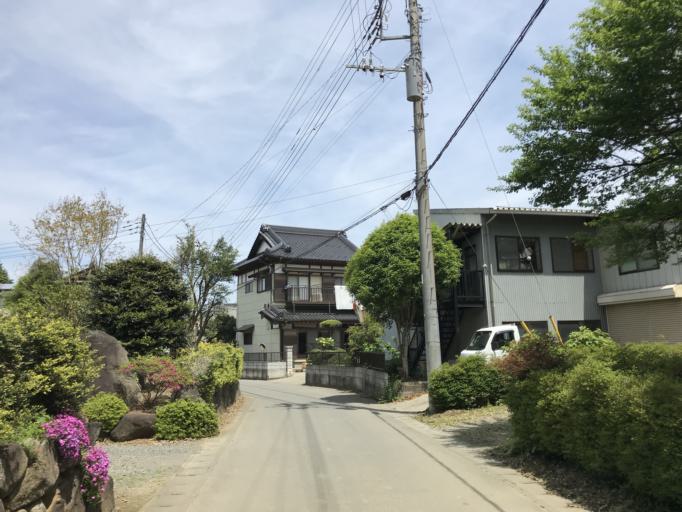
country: JP
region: Ibaraki
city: Mitsukaido
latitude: 35.9882
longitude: 139.9700
